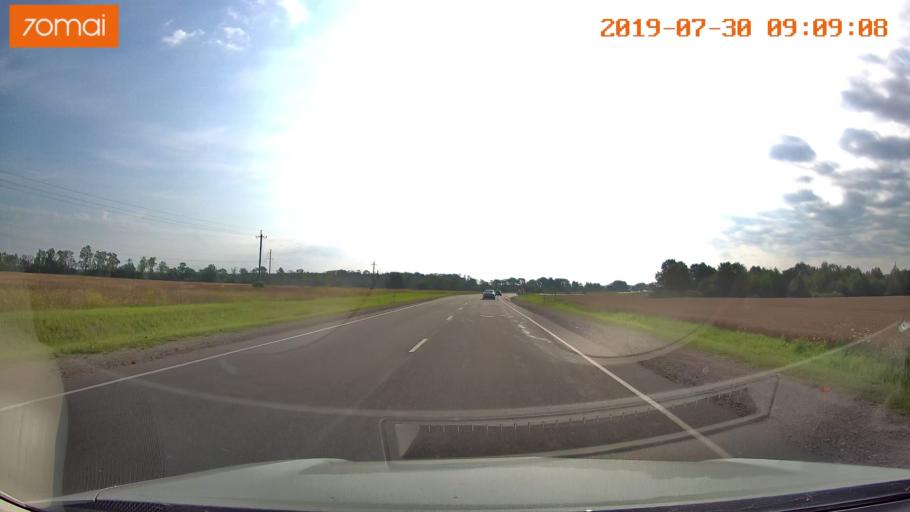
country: RU
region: Kaliningrad
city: Nesterov
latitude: 54.6137
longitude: 22.4025
